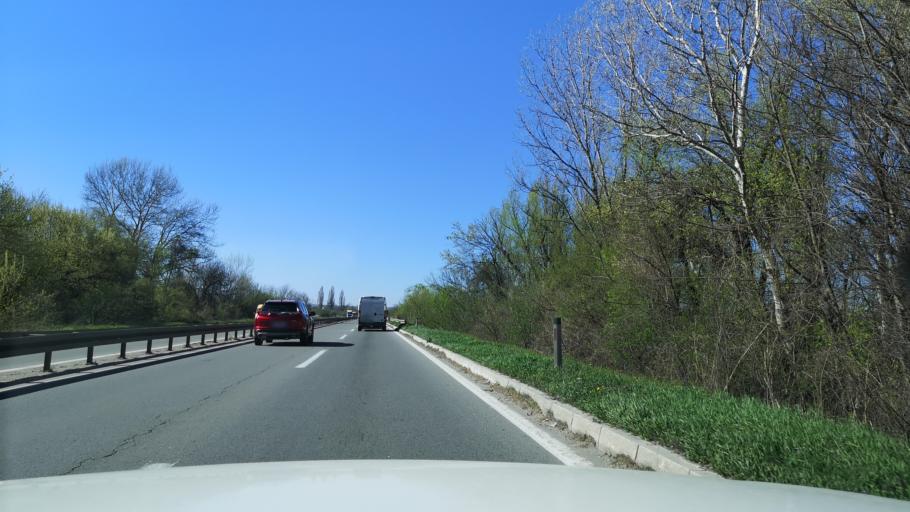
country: RS
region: Central Serbia
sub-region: Belgrade
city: Cukarica
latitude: 44.7660
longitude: 20.3915
